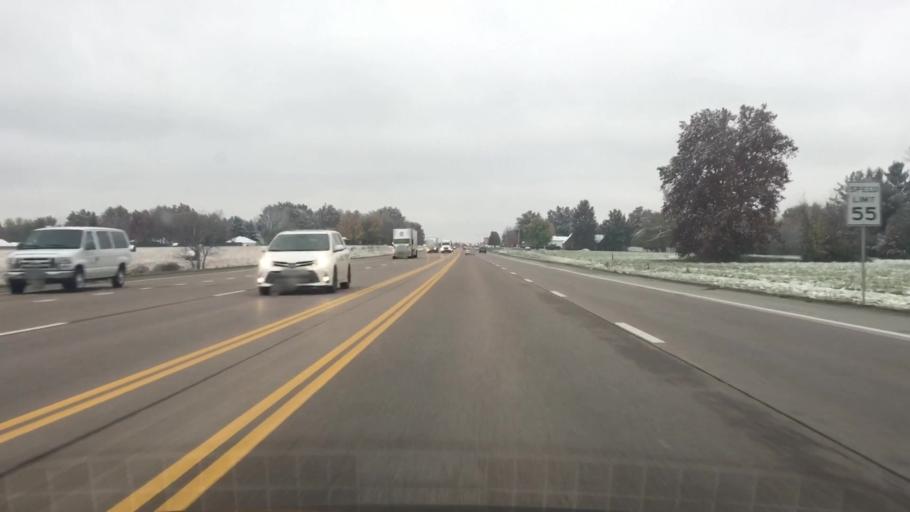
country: US
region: Missouri
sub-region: Henry County
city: Clinton
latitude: 38.3773
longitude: -93.7516
